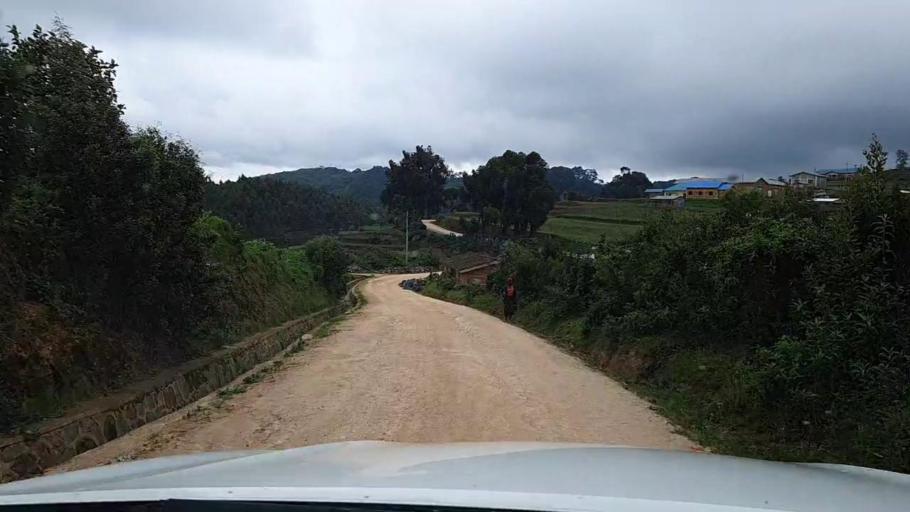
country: RW
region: Southern Province
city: Nzega
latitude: -2.3771
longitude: 29.3825
